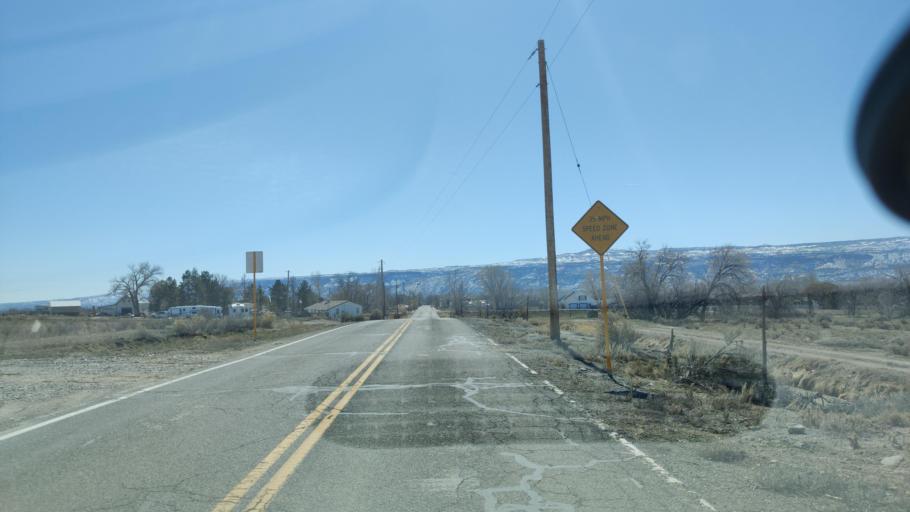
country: US
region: Colorado
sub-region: Mesa County
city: Fruita
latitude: 39.1745
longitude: -108.7105
